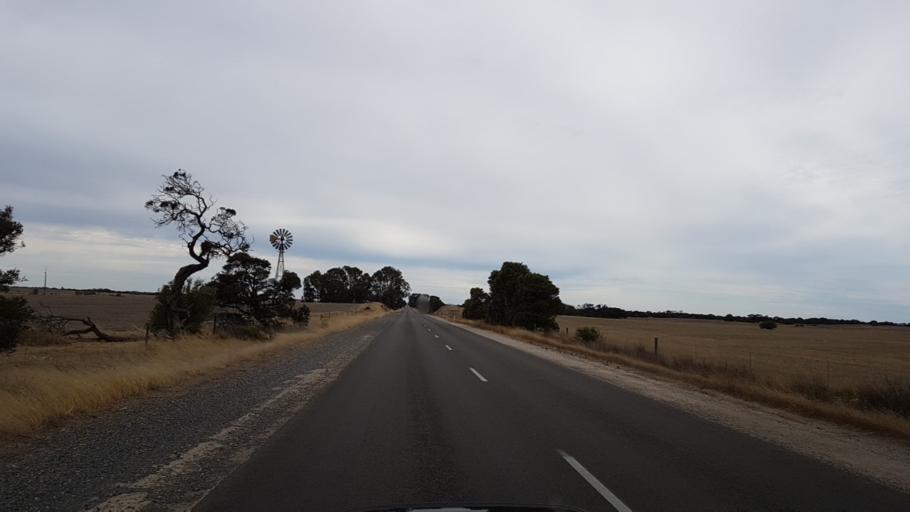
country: AU
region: South Australia
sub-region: Yorke Peninsula
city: Honiton
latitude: -34.9851
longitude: 137.1755
